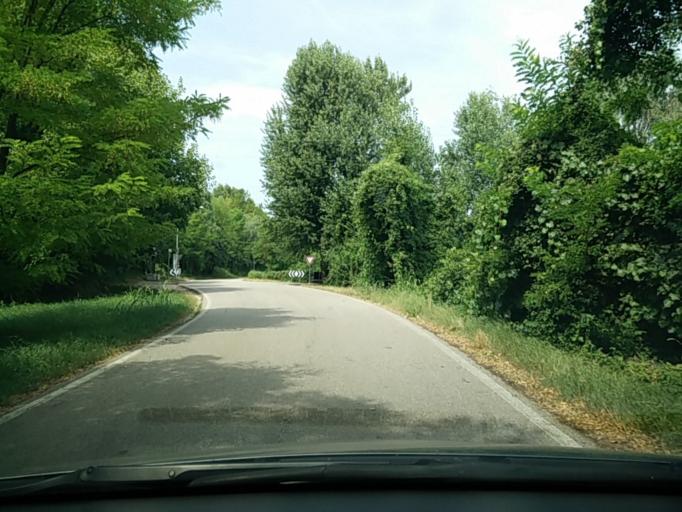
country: IT
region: Veneto
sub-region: Provincia di Treviso
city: Silea
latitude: 45.6508
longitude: 12.2876
